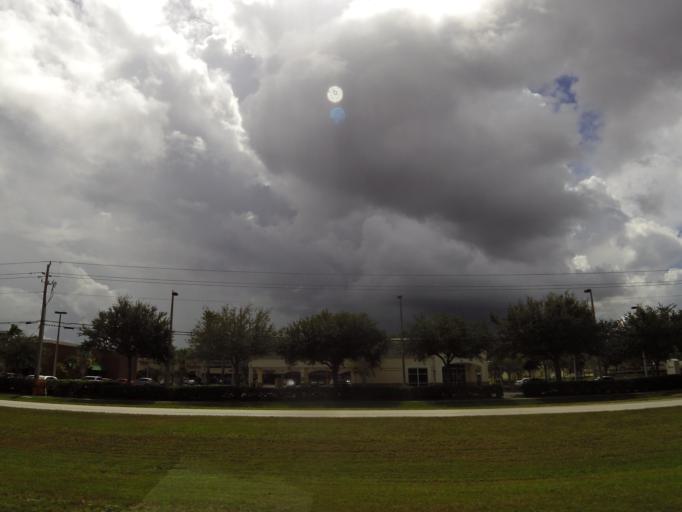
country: US
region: Florida
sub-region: Clay County
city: Lakeside
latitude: 30.1024
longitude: -81.7166
